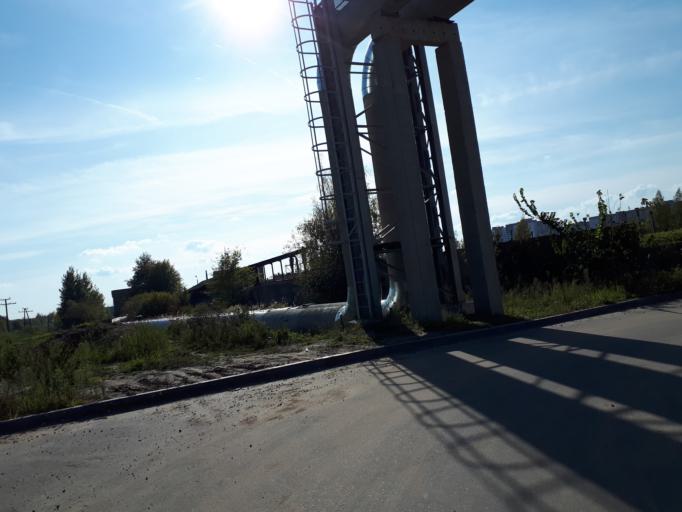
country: BY
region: Vitebsk
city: Vitebsk
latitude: 55.1636
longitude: 30.2443
